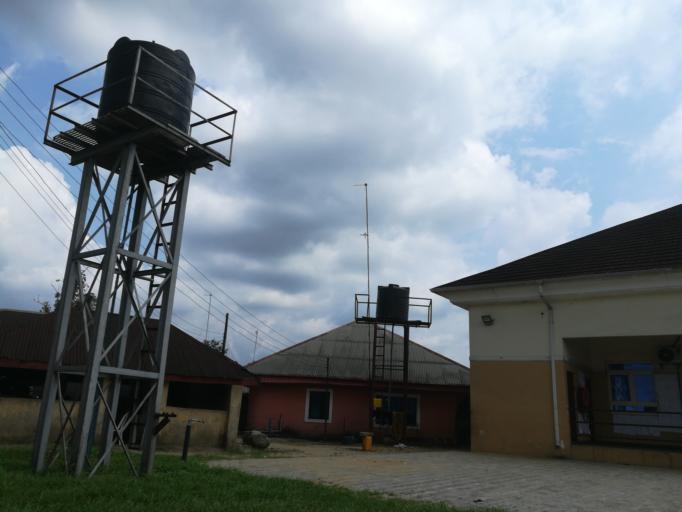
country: NG
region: Rivers
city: Okrika
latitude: 4.7251
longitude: 7.1531
